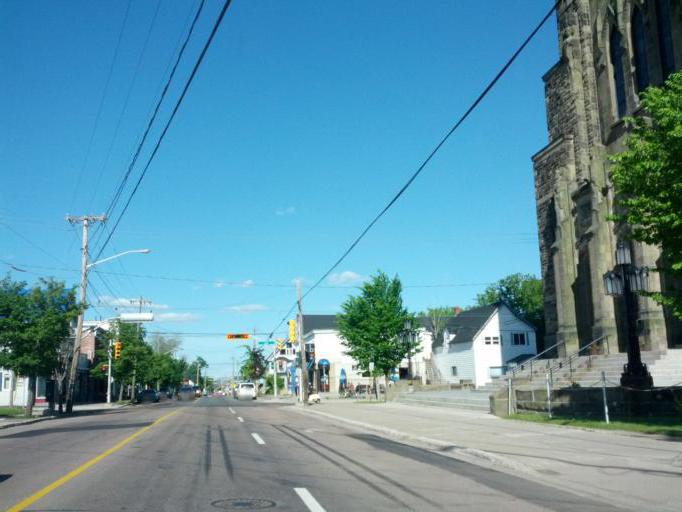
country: CA
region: New Brunswick
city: Moncton
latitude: 46.0913
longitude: -64.7825
